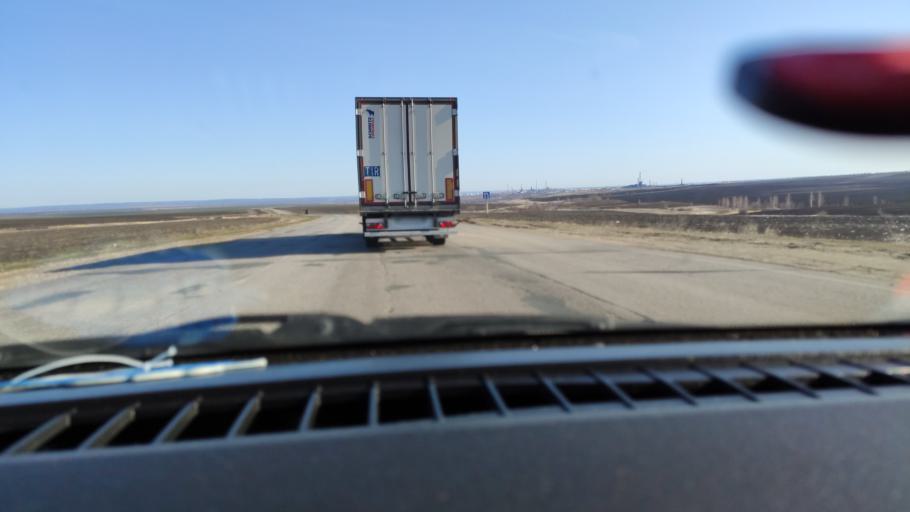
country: RU
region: Samara
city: Syzran'
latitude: 53.0046
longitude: 48.3313
